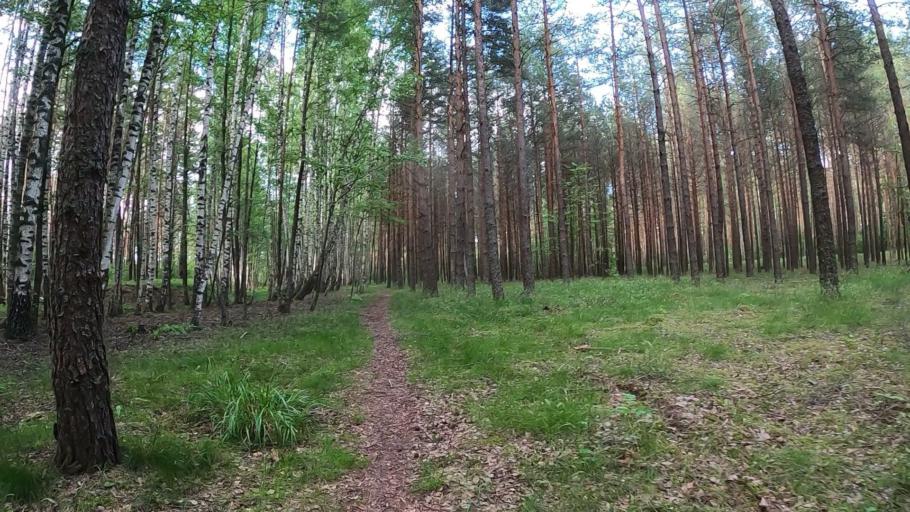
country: LV
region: Riga
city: Jaunciems
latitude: 57.0626
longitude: 24.1312
